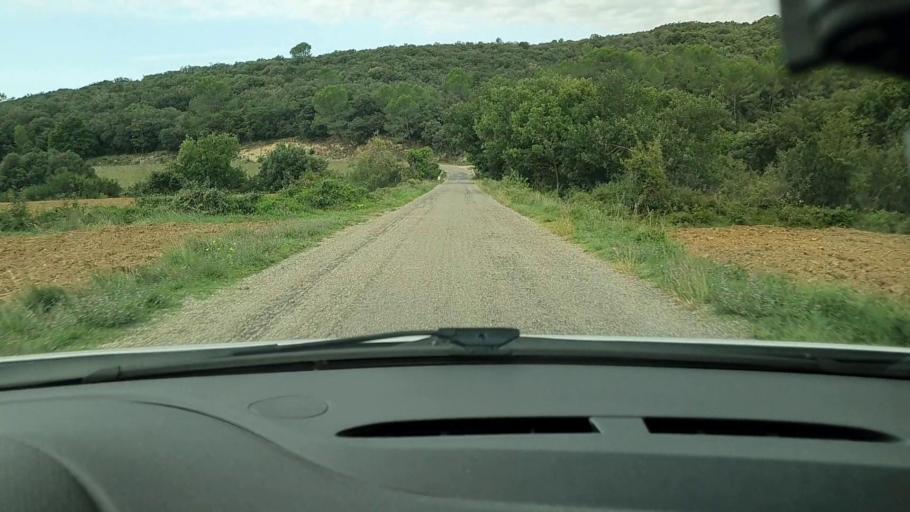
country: FR
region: Languedoc-Roussillon
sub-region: Departement du Gard
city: Montaren-et-Saint-Mediers
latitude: 44.0757
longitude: 4.3124
